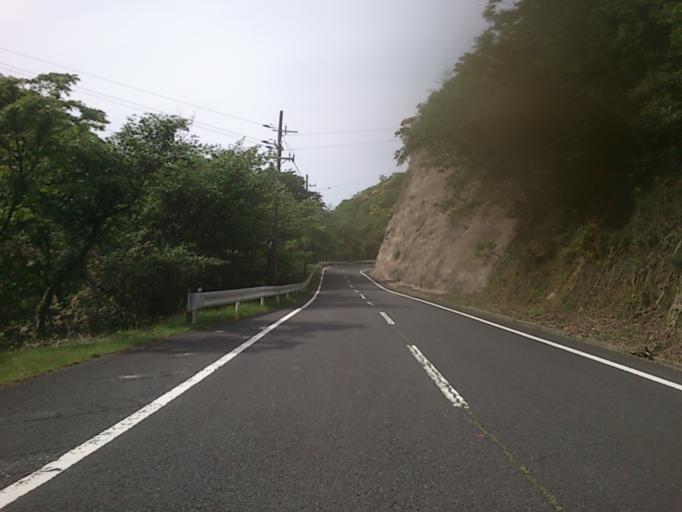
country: JP
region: Hyogo
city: Toyooka
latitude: 35.6835
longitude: 134.9875
